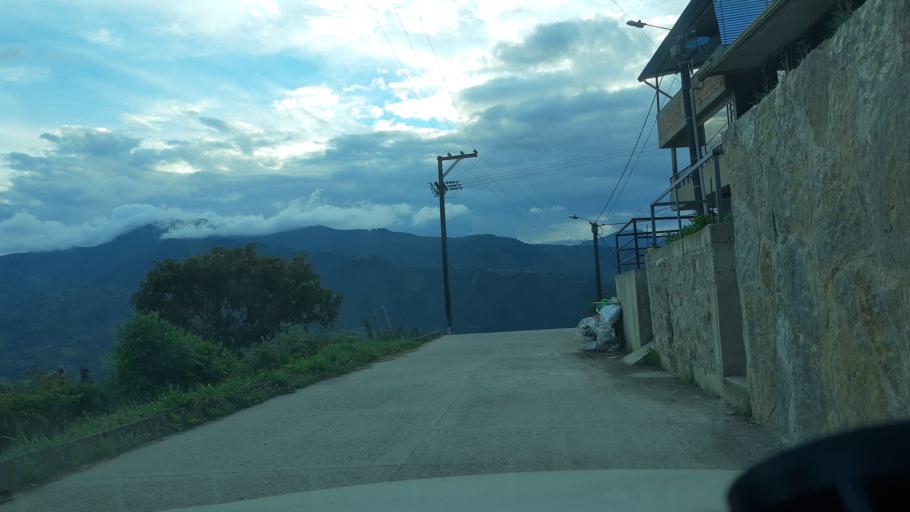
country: CO
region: Boyaca
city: Chivor
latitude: 4.9705
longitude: -73.3221
